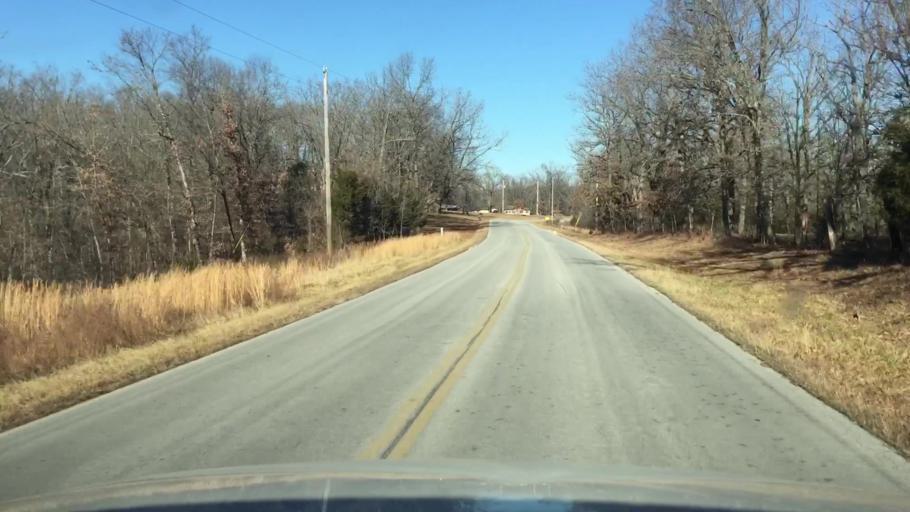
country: US
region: Missouri
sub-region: Morgan County
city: Versailles
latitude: 38.3338
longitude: -92.7684
